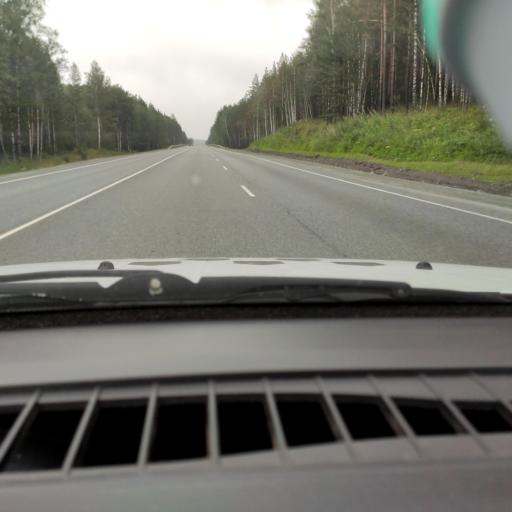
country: RU
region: Chelyabinsk
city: Zlatoust
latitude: 55.0562
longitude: 59.6766
